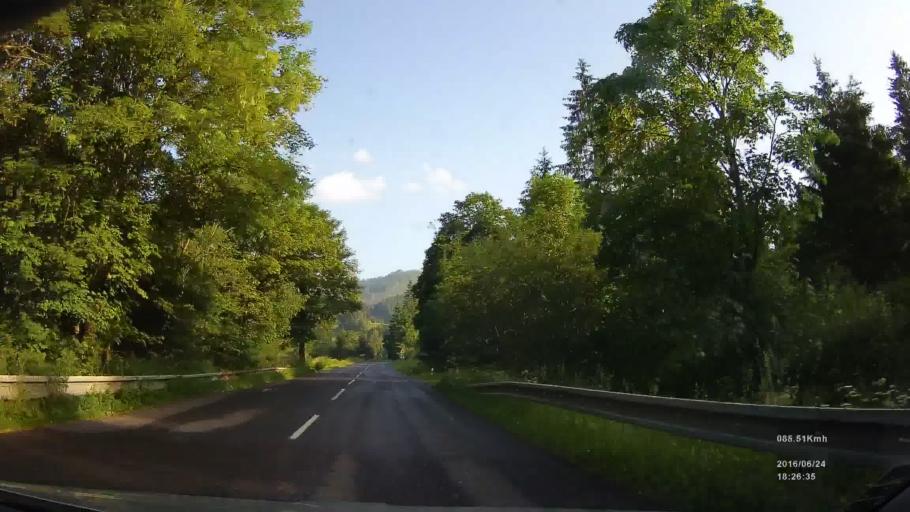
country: SK
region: Zilinsky
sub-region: Okres Zilina
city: Liptovsky Hradok
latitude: 48.9555
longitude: 19.7732
